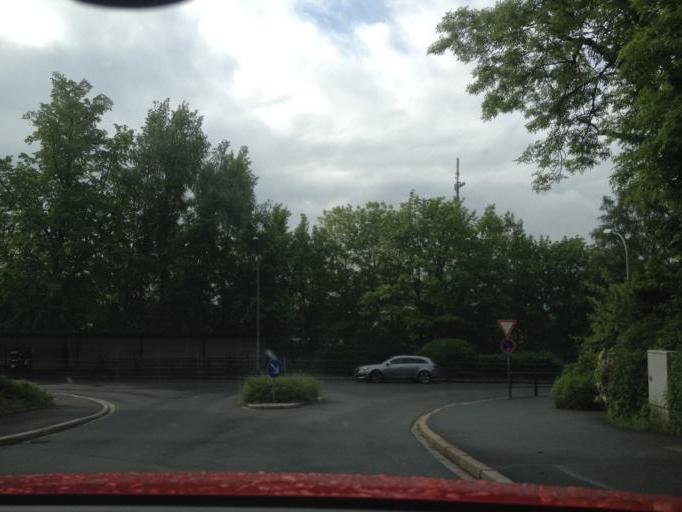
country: DE
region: Bavaria
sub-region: Regierungsbezirk Mittelfranken
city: Lauf an der Pegnitz
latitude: 49.5134
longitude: 11.2777
